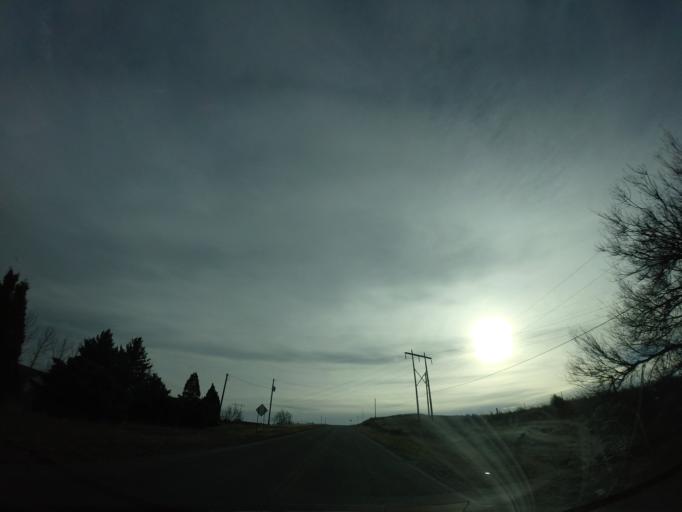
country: US
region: Montana
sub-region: Yellowstone County
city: Billings
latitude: 45.7935
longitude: -108.4555
